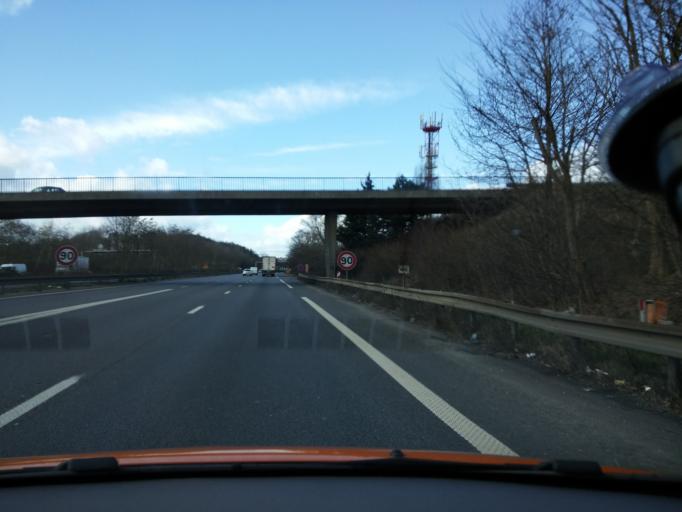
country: FR
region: Ile-de-France
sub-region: Departement de l'Essonne
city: Champlan
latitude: 48.7132
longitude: 2.2816
